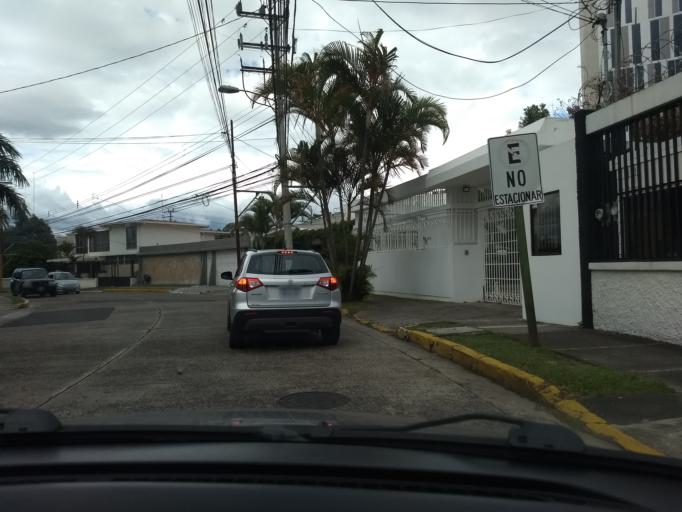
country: CR
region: San Jose
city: San Jose
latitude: 9.9381
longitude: -84.1103
